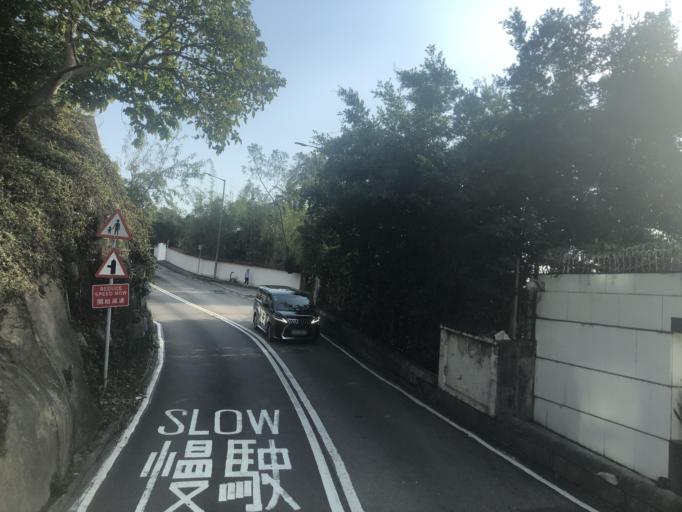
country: HK
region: Wanchai
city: Wan Chai
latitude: 22.2412
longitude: 114.1872
